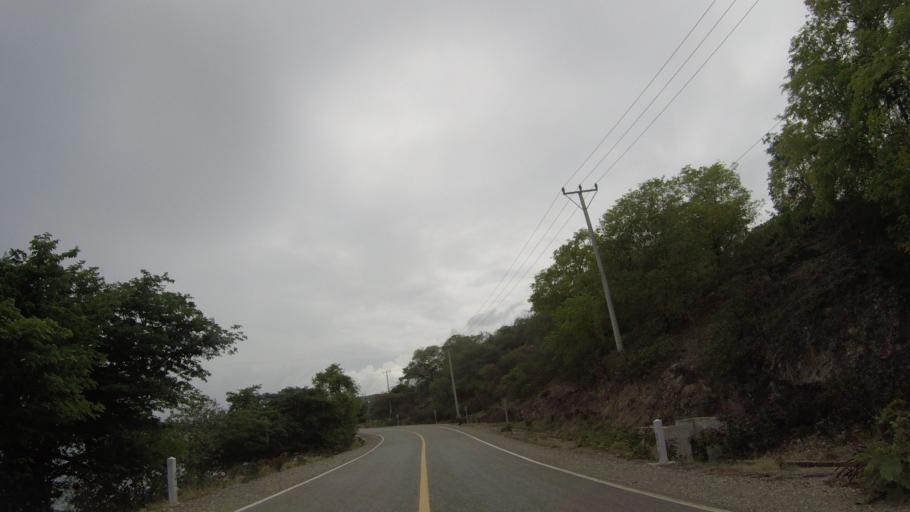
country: TL
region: Lautem
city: Lospalos
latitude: -8.4180
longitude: 126.7789
